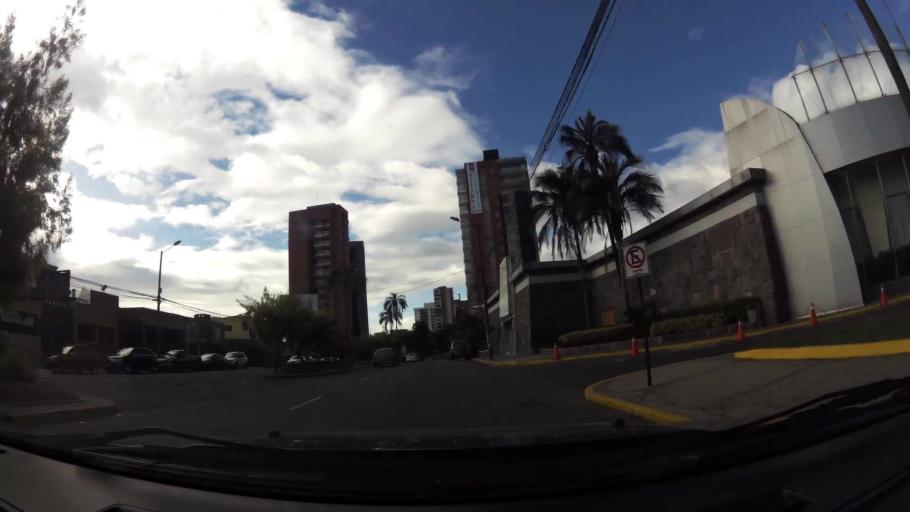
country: EC
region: Pichincha
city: Quito
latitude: -0.2017
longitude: -78.4802
